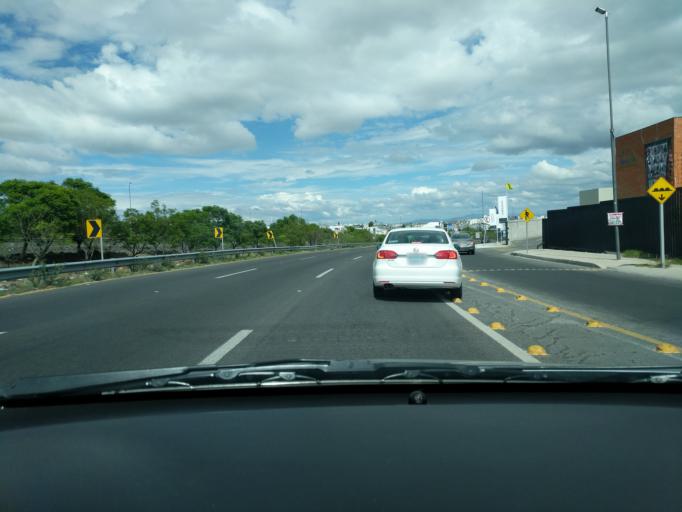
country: MX
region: Queretaro
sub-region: El Marques
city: La Pradera
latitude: 20.6608
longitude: -100.3455
